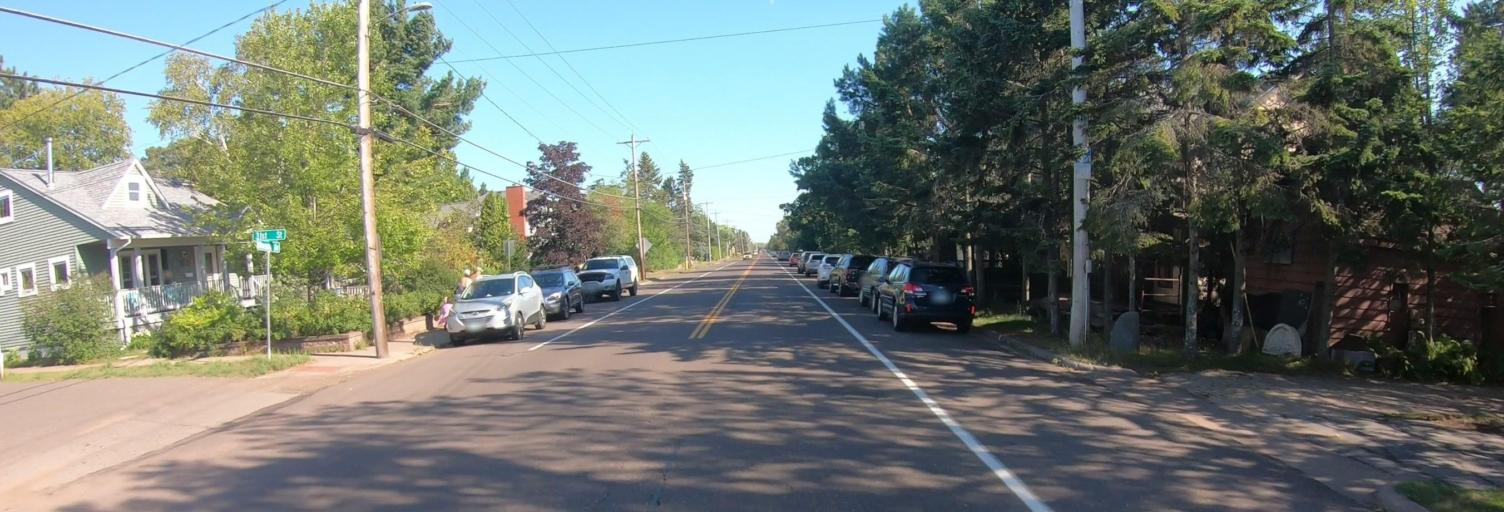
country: US
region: Wisconsin
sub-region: Douglas County
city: Superior
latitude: 46.7515
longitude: -92.0724
